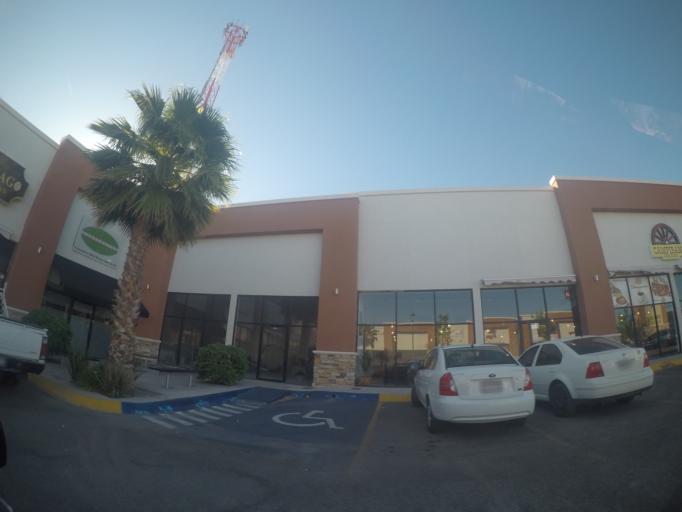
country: MX
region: Chihuahua
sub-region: Chihuahua
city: Chihuahua
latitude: 28.6696
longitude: -106.0939
